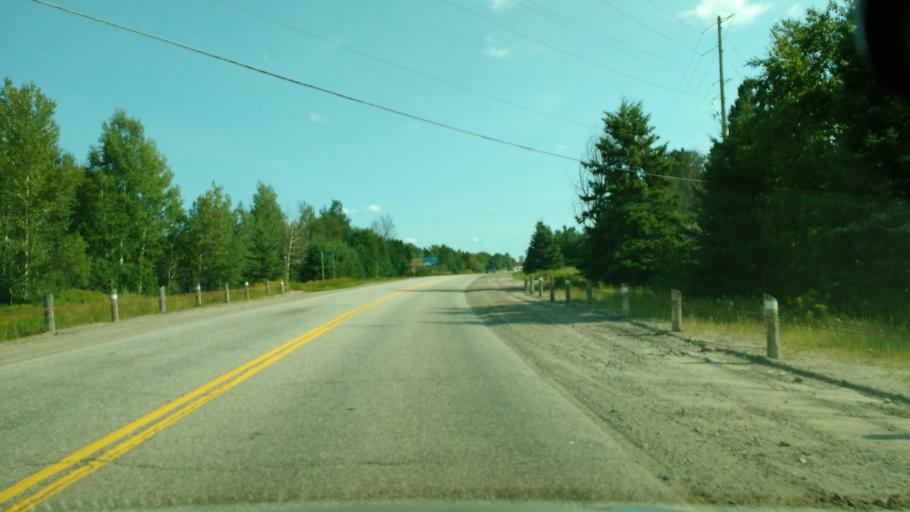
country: CA
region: Ontario
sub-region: Nipissing District
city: North Bay
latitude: 46.2564
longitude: -79.3857
